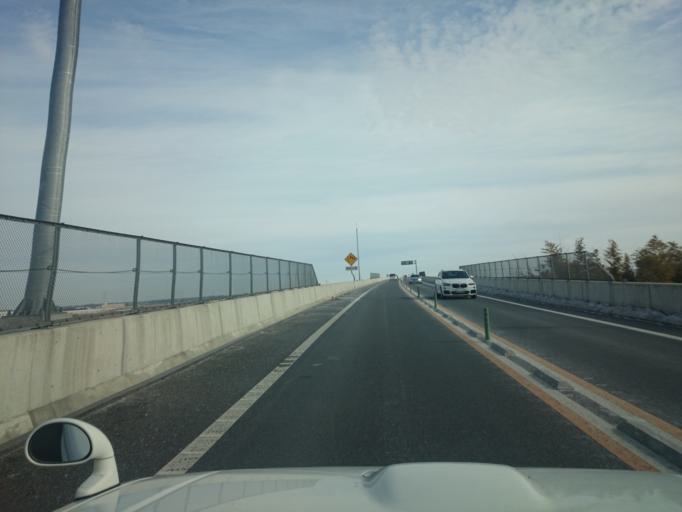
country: JP
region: Ibaraki
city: Sakai
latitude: 36.1125
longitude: 139.7605
